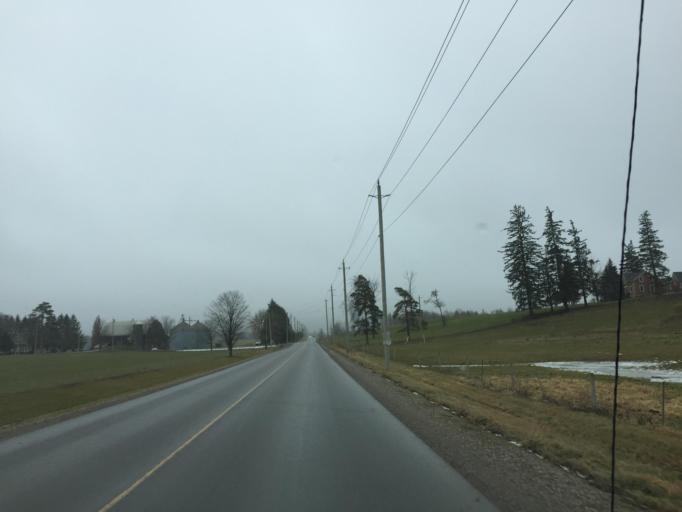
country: CA
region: Ontario
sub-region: Wellington County
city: Guelph
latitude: 43.4794
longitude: -80.3356
